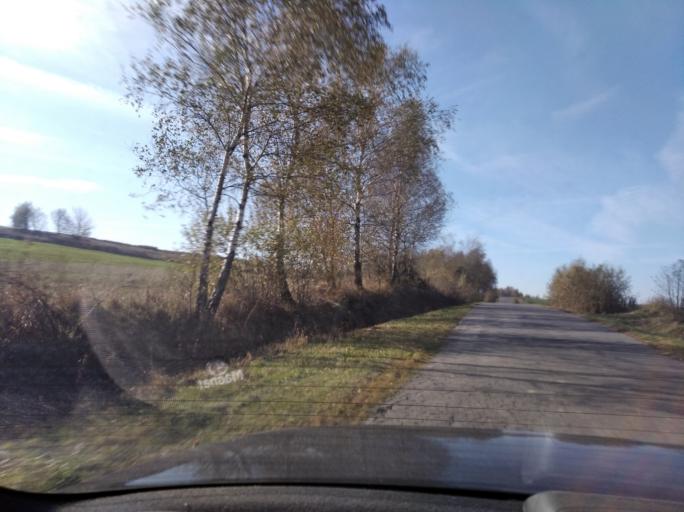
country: PL
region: Subcarpathian Voivodeship
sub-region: Powiat ropczycko-sedziszowski
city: Wielopole Skrzynskie
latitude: 49.9012
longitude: 21.5823
